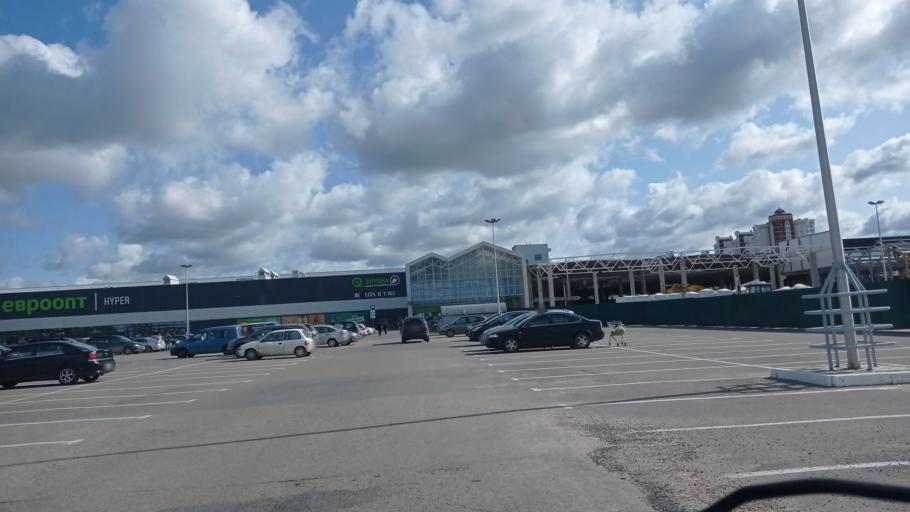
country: BY
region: Vitebsk
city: Vitebsk
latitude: 55.1750
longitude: 30.2637
